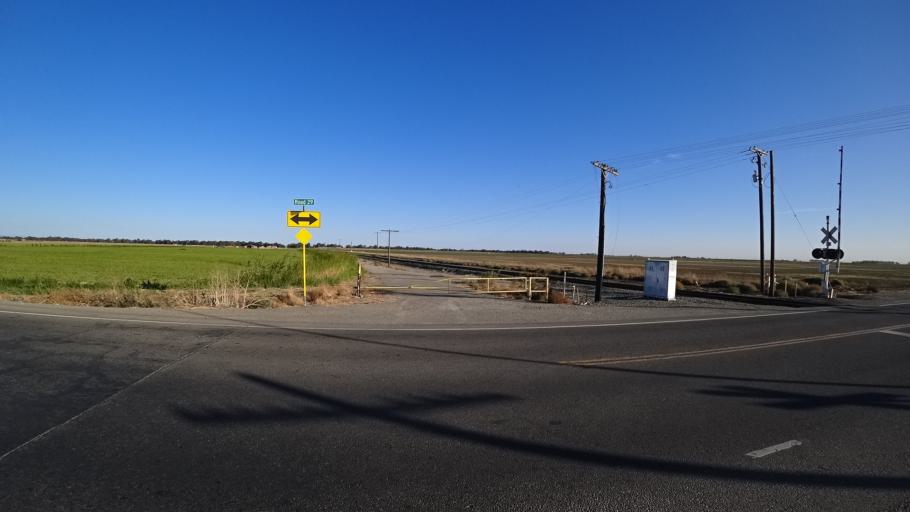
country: US
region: California
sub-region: Yolo County
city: Davis
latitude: 38.5901
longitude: -121.7525
